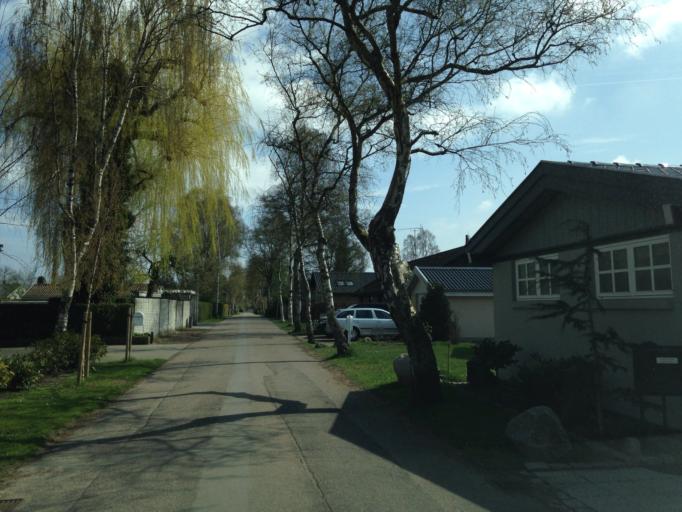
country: DK
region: Zealand
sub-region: Greve Kommune
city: Greve
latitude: 55.5777
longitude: 12.2896
